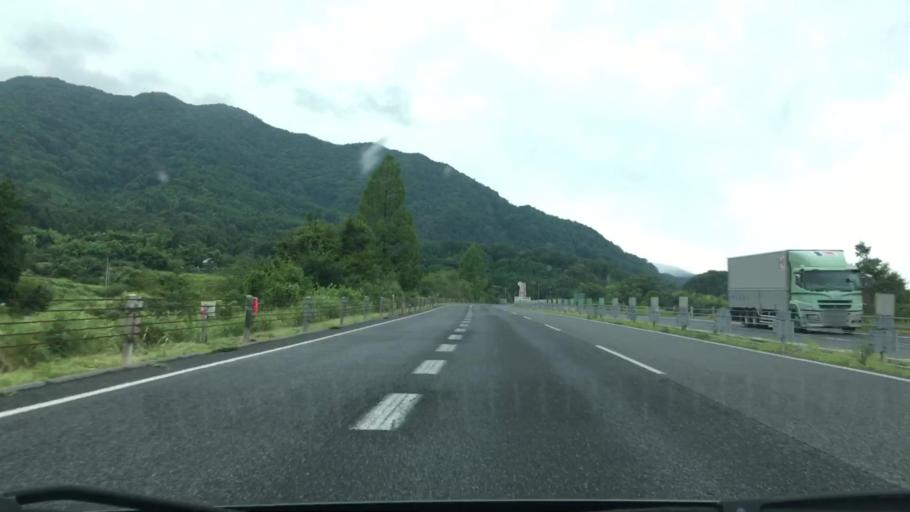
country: JP
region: Hiroshima
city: Hiroshima-shi
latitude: 34.6364
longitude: 132.5142
